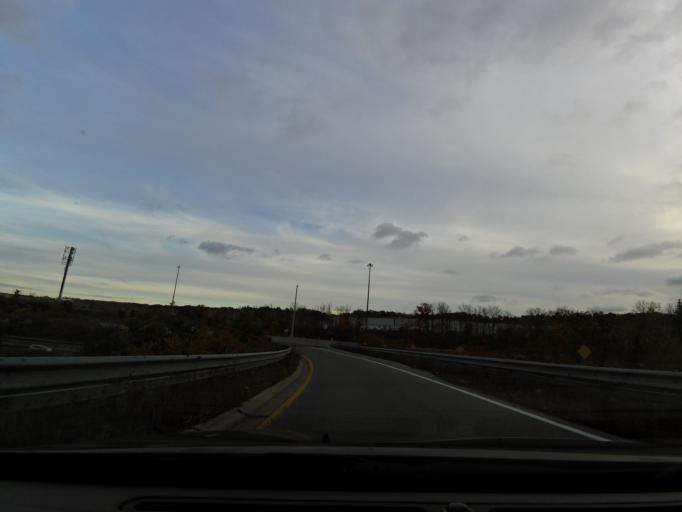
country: CA
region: Ontario
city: Hamilton
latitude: 43.2562
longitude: -79.9077
